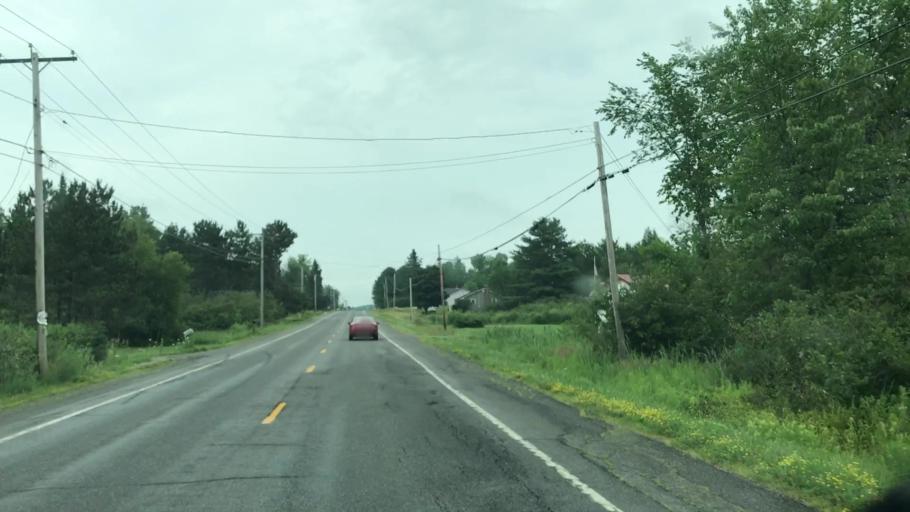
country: US
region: Maine
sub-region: Penobscot County
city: Lincoln
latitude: 45.3485
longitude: -68.5466
